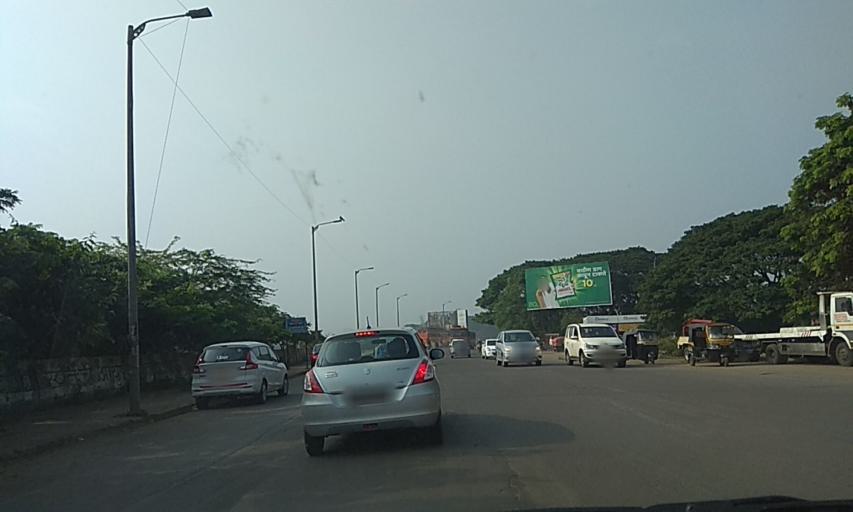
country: IN
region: Maharashtra
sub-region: Pune Division
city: Shivaji Nagar
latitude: 18.5351
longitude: 73.8617
